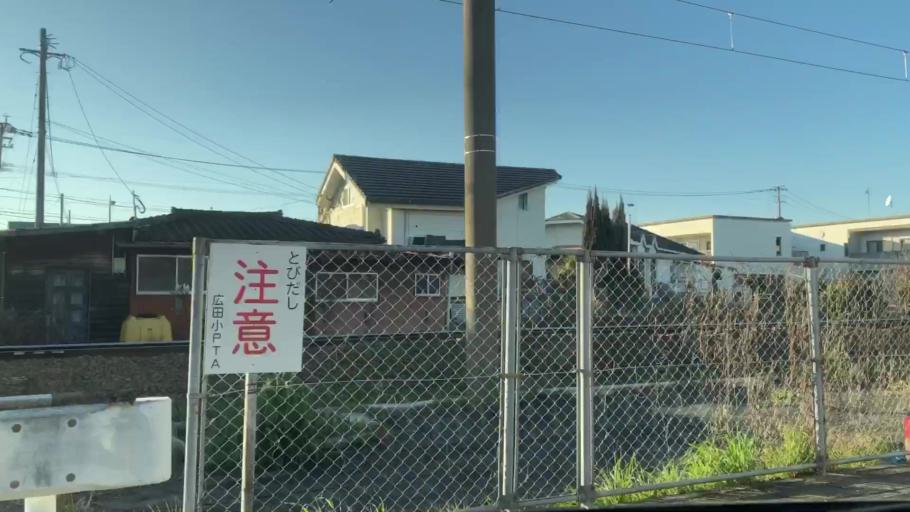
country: JP
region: Nagasaki
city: Sasebo
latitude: 33.1293
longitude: 129.7990
